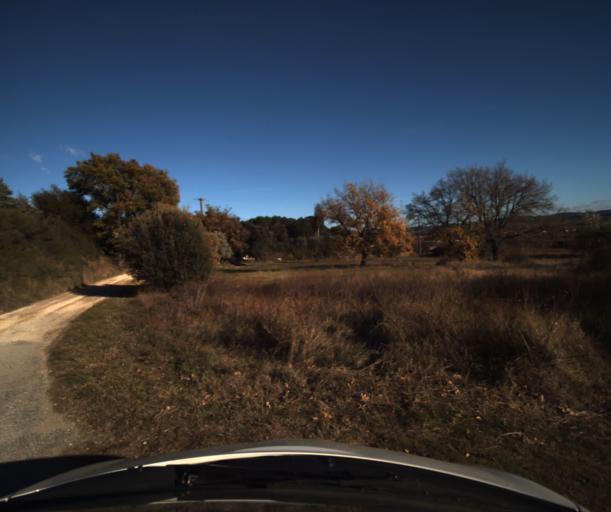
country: FR
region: Provence-Alpes-Cote d'Azur
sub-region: Departement du Vaucluse
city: Pertuis
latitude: 43.7092
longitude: 5.4852
